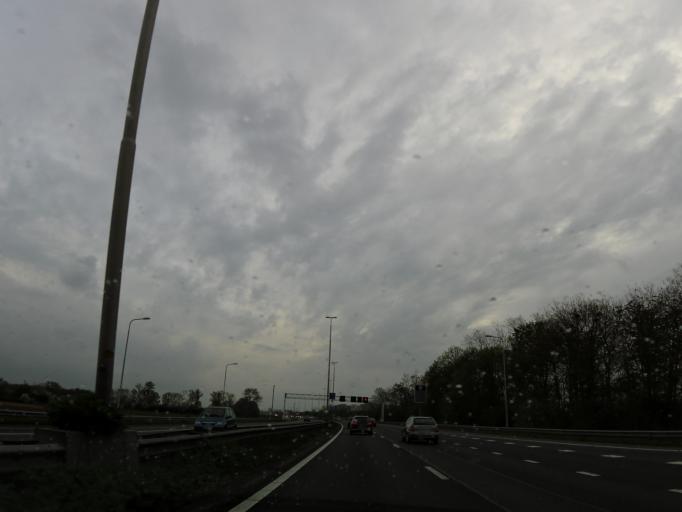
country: NL
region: Limburg
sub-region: Gemeente Maasgouw
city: Maasbracht
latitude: 51.1026
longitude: 5.8475
